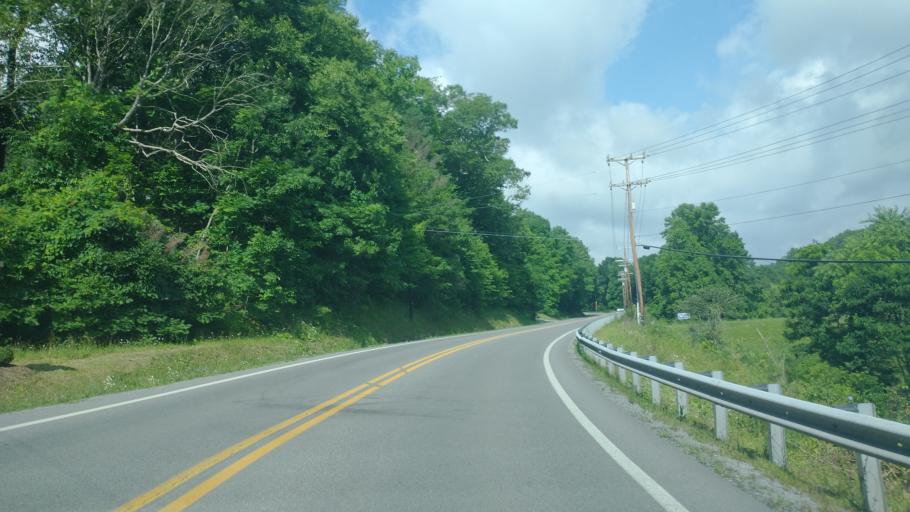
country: US
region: West Virginia
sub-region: Mercer County
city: Princeton
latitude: 37.3603
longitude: -81.1301
